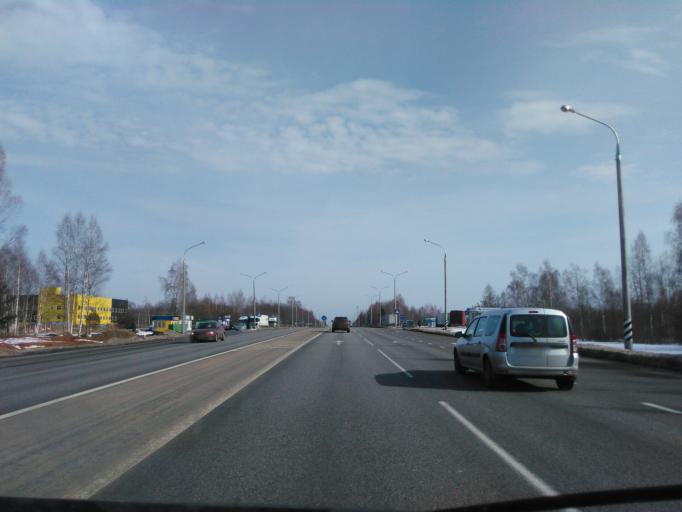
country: RU
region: Smolensk
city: Rudnya
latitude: 54.6904
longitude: 30.9661
